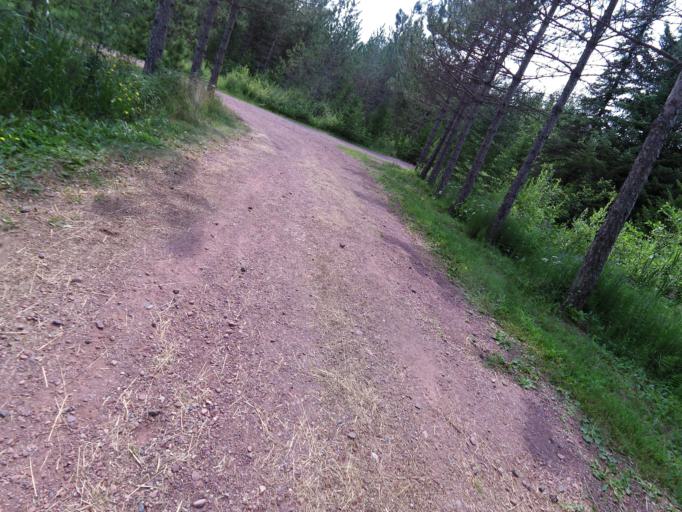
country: CA
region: Ontario
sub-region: Thunder Bay District
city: Thunder Bay
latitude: 48.7956
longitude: -88.6200
